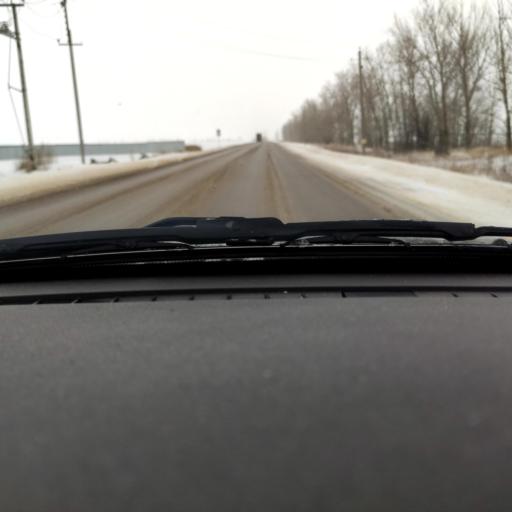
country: RU
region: Voronezj
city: Novaya Usman'
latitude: 51.6006
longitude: 39.3735
